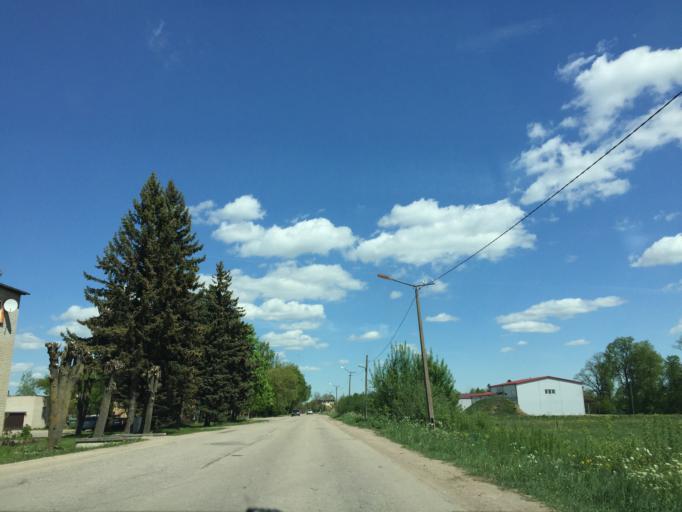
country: LV
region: Bauskas Rajons
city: Bauska
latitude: 56.4114
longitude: 24.1740
